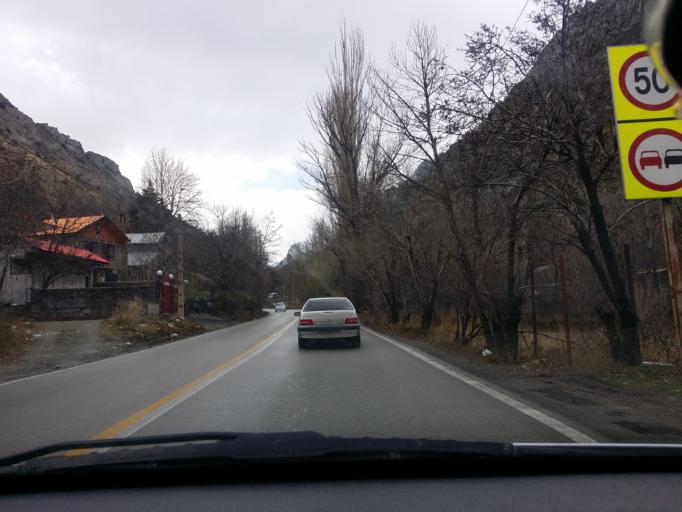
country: IR
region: Tehran
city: Tajrish
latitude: 36.0247
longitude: 51.2569
